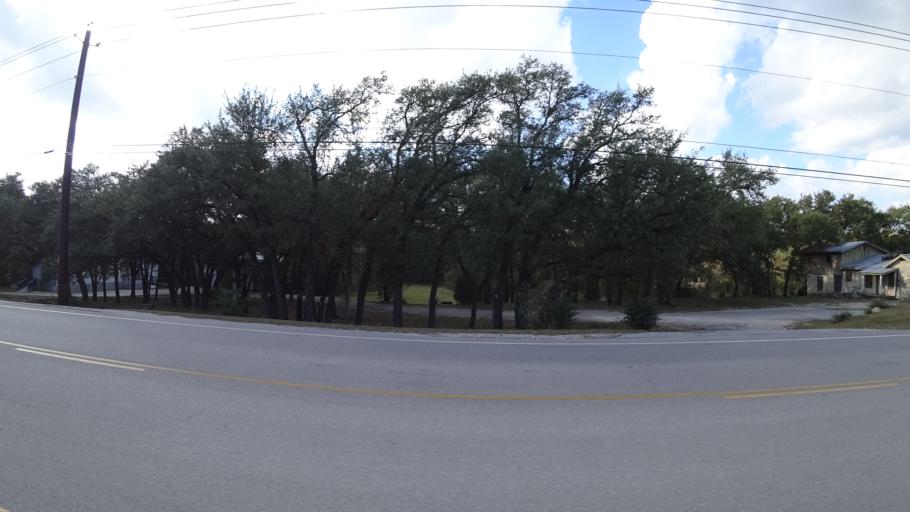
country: US
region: Texas
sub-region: Travis County
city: Barton Creek
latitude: 30.2649
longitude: -97.8890
